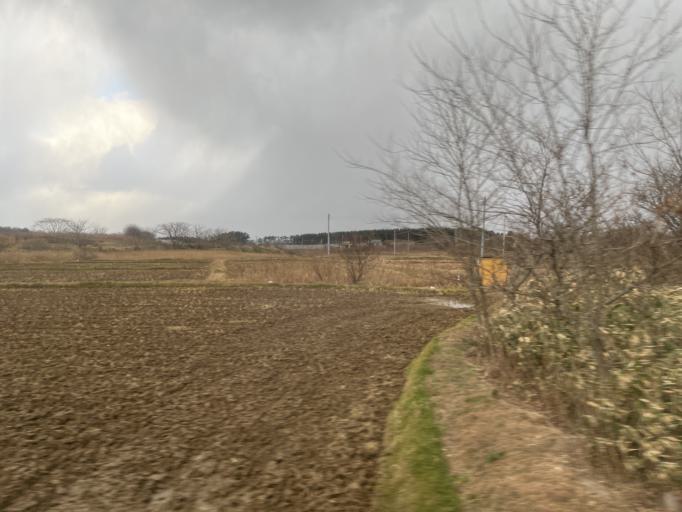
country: JP
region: Aomori
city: Mutsu
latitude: 41.1347
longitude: 141.2796
